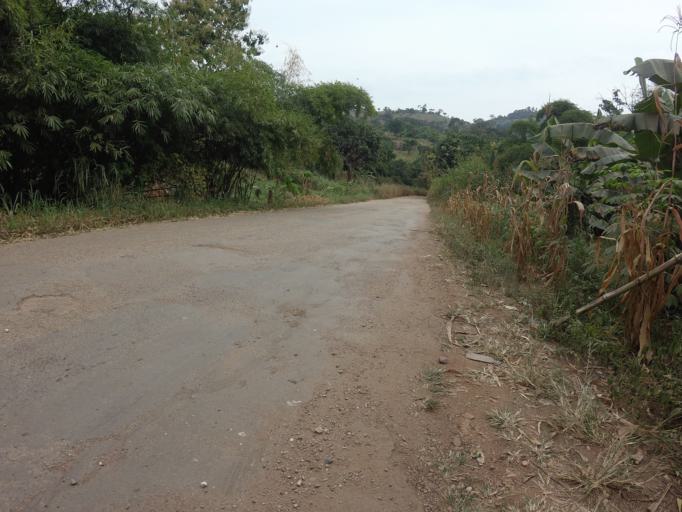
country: GH
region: Volta
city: Ho
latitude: 6.6860
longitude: 0.3453
